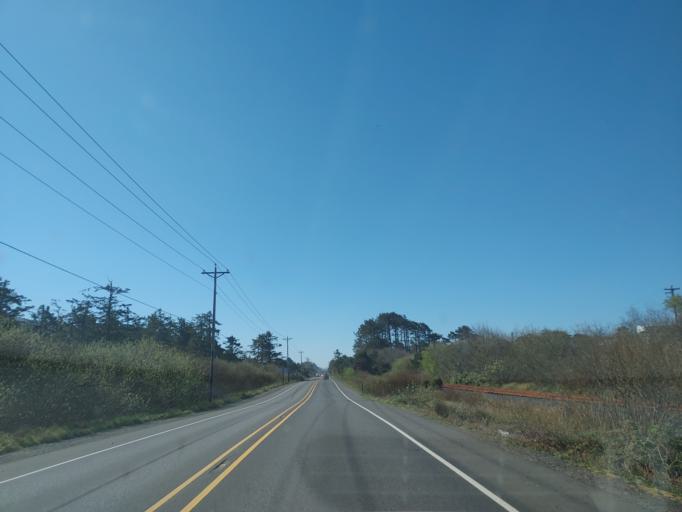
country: US
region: Oregon
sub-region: Tillamook County
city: Rockaway Beach
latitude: 45.6033
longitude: -123.9456
